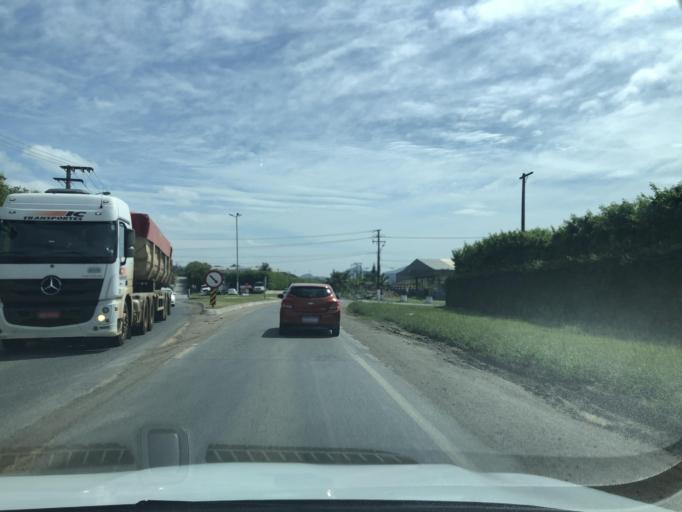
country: BR
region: Santa Catarina
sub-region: Sao Francisco Do Sul
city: Sao Francisco do Sul
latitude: -26.2573
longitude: -48.6226
